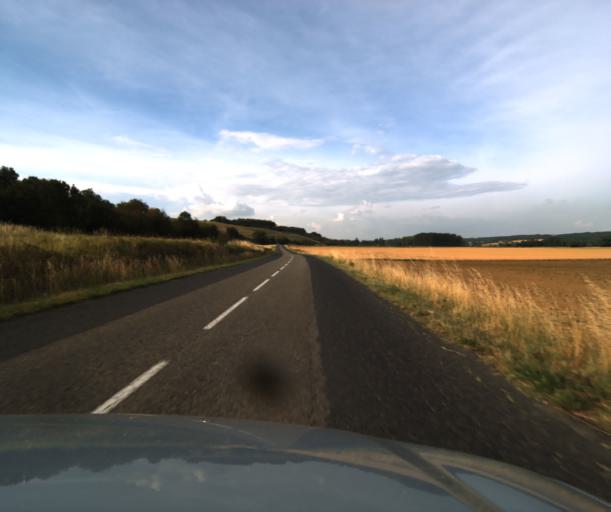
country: FR
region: Midi-Pyrenees
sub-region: Departement du Tarn-et-Garonne
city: Castelsarrasin
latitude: 43.9601
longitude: 1.1043
